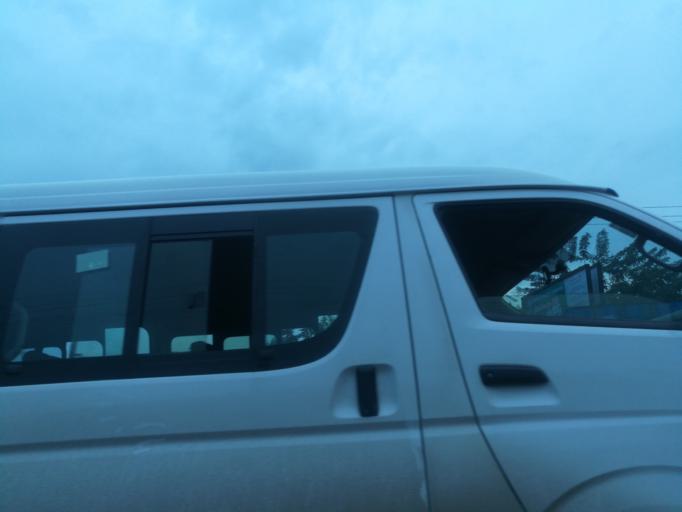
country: NG
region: Oyo
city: Ibadan
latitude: 7.3991
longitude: 3.9491
